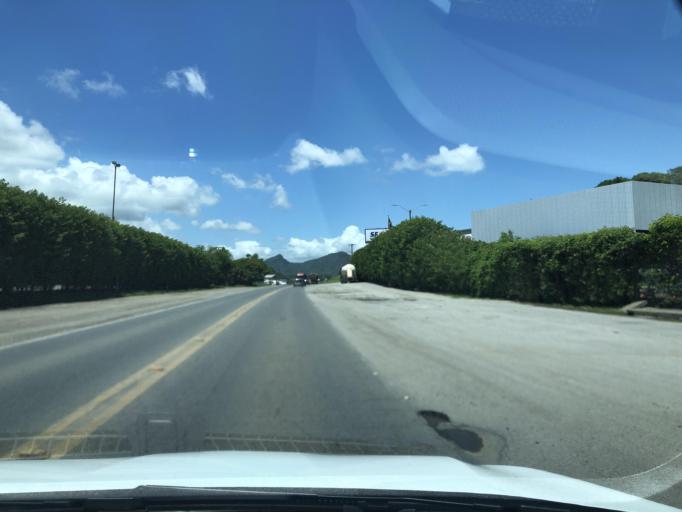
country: BR
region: Santa Catarina
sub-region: Sao Francisco Do Sul
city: Sao Francisco do Sul
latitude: -26.2591
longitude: -48.6245
